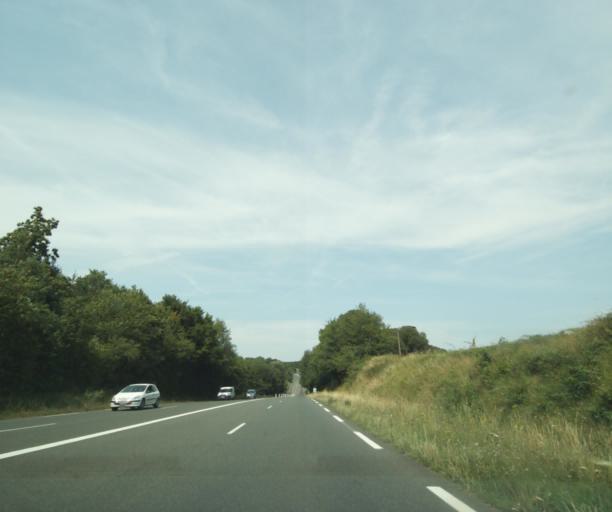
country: FR
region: Centre
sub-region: Departement d'Indre-et-Loire
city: Sainte-Maure-de-Touraine
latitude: 47.1391
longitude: 0.6404
